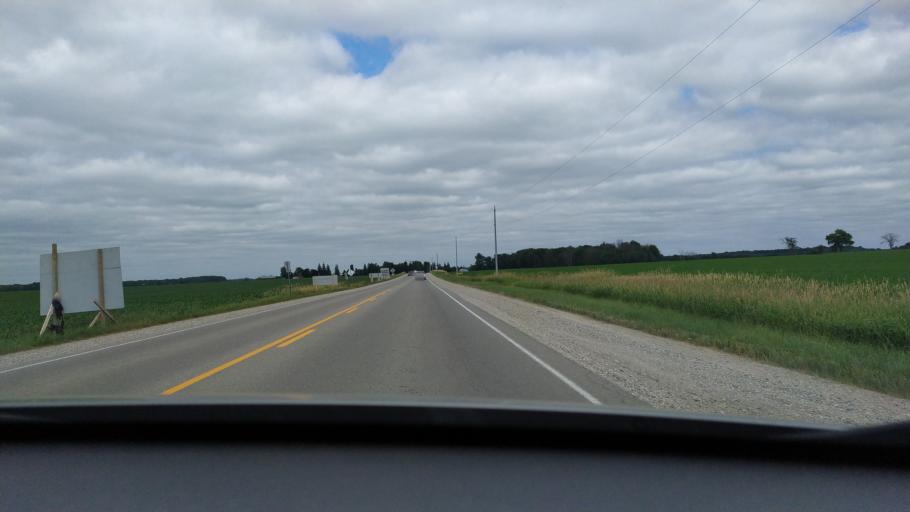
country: CA
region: Ontario
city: Stratford
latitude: 43.3163
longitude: -80.9826
